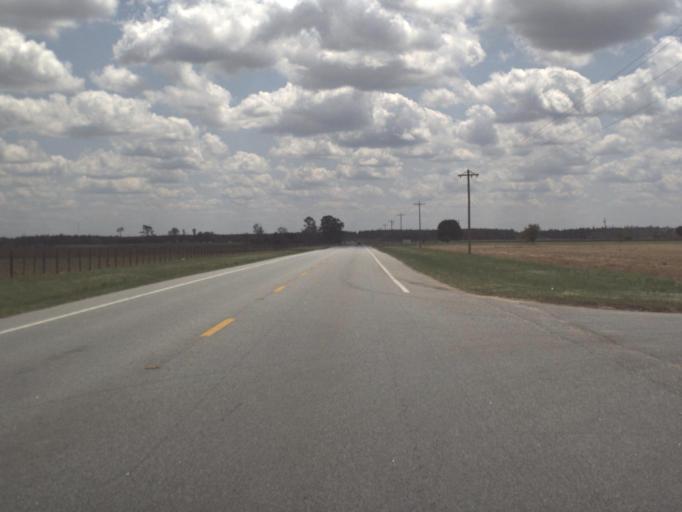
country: US
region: Alabama
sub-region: Escambia County
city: Atmore
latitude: 30.9418
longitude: -87.4877
